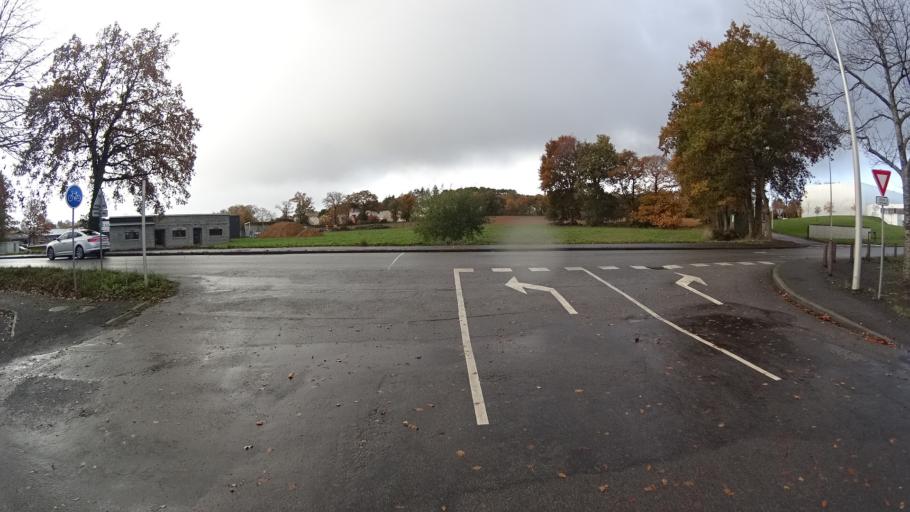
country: FR
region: Brittany
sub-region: Departement d'Ille-et-Vilaine
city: Redon
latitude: 47.6682
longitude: -2.0759
